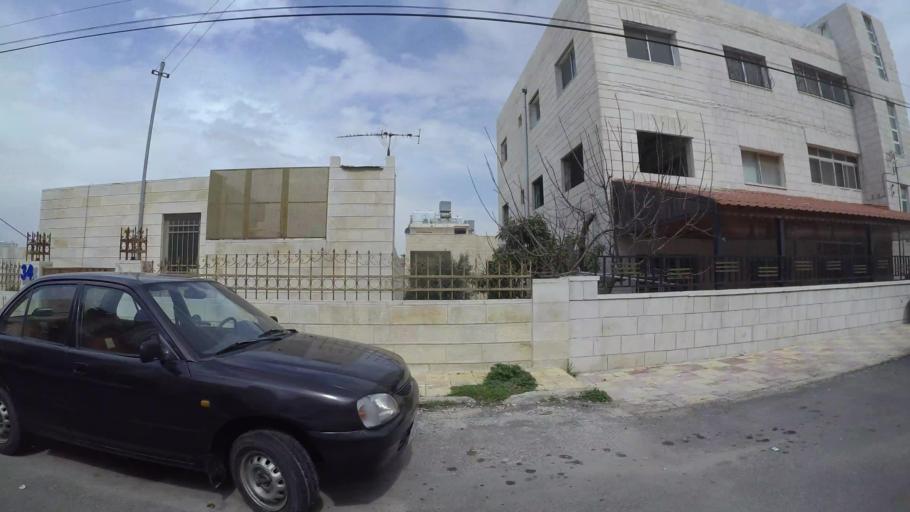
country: JO
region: Amman
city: Umm as Summaq
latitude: 31.8985
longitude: 35.8376
